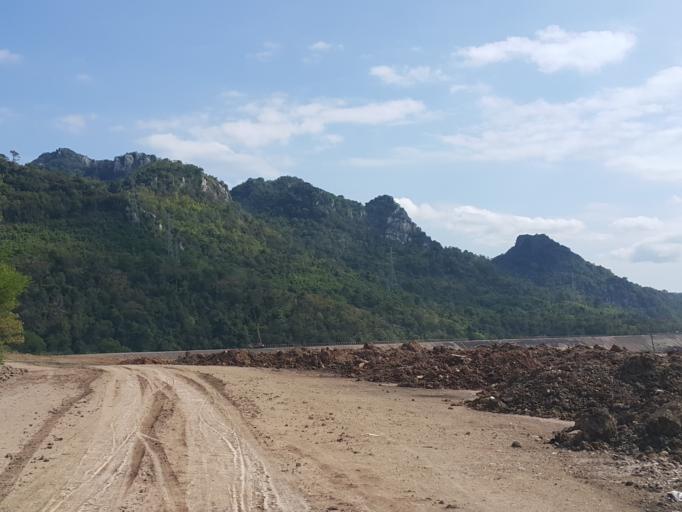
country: TH
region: Lampang
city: Mae Mo
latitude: 18.3291
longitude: 99.7590
